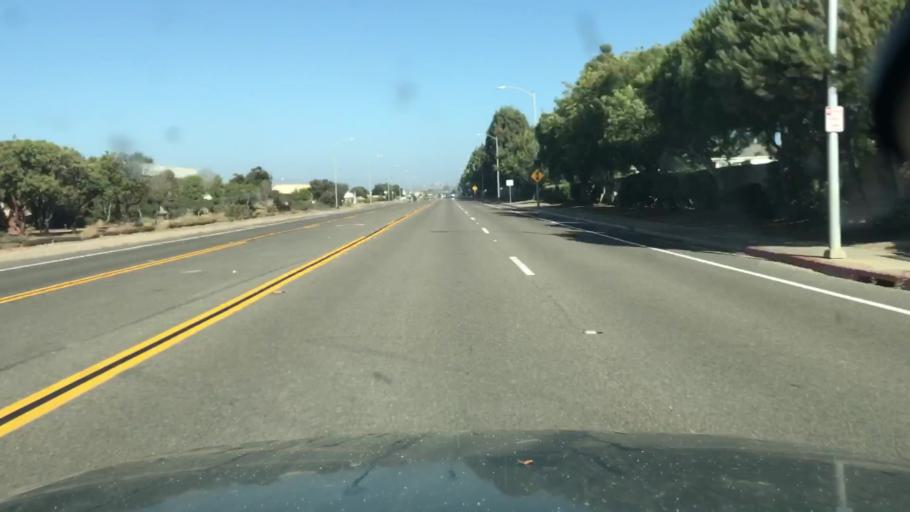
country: US
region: California
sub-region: Santa Barbara County
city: Lompoc
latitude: 34.6610
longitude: -120.4797
